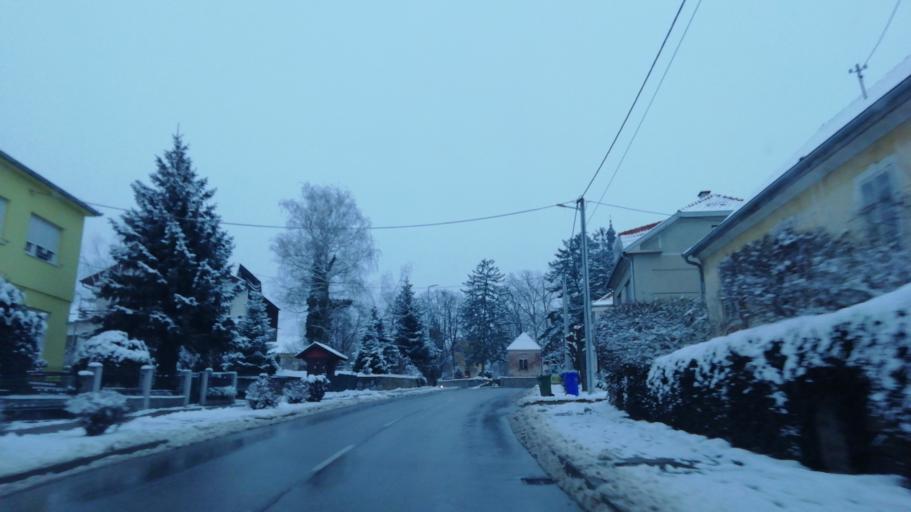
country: HR
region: Zagrebacka
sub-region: Grad Vrbovec
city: Vrbovec
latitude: 45.8833
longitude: 16.4157
